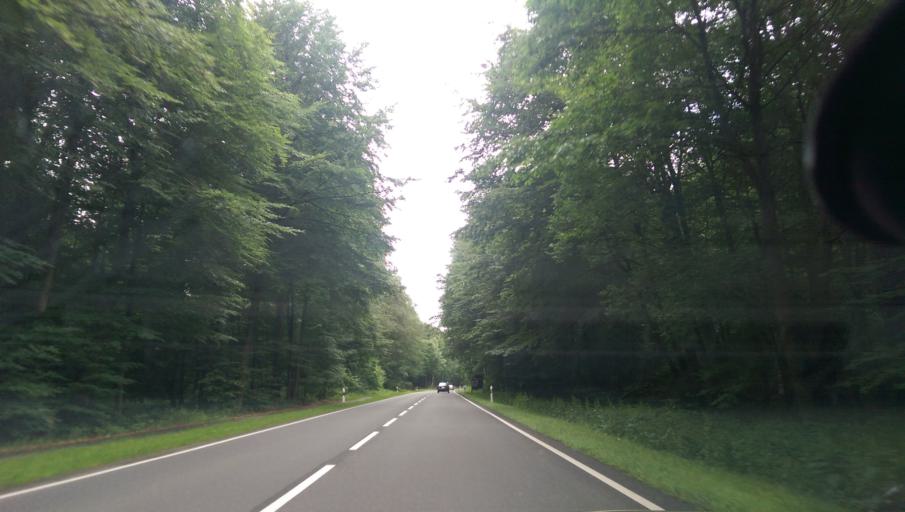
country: DE
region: Lower Saxony
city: Botersen
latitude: 53.1412
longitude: 9.3501
